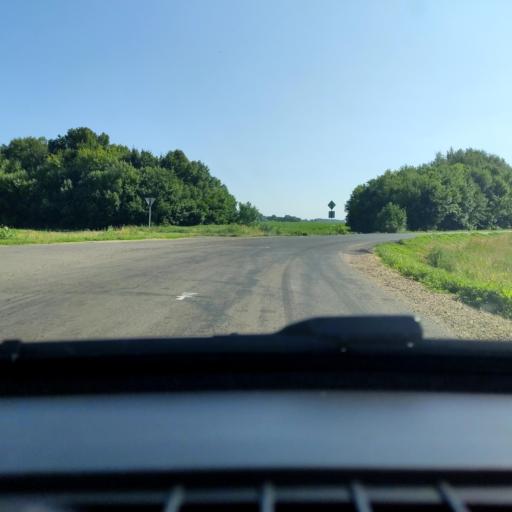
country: RU
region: Voronezj
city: Anna
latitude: 51.6343
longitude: 40.3570
